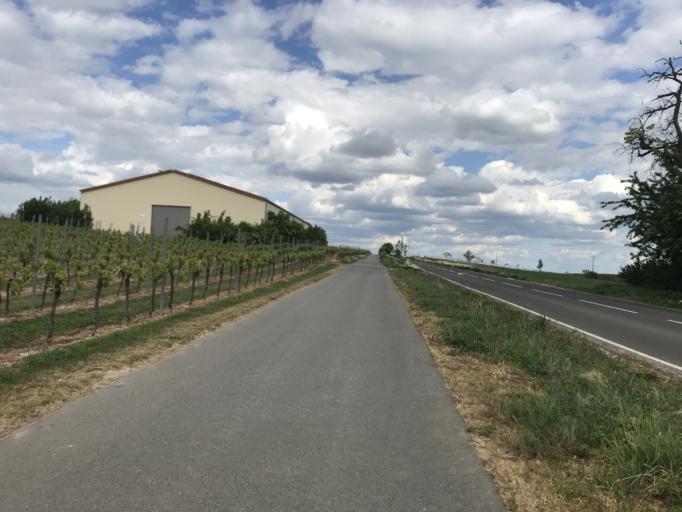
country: DE
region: Rheinland-Pfalz
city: Lorzweiler
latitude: 49.9028
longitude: 8.3087
